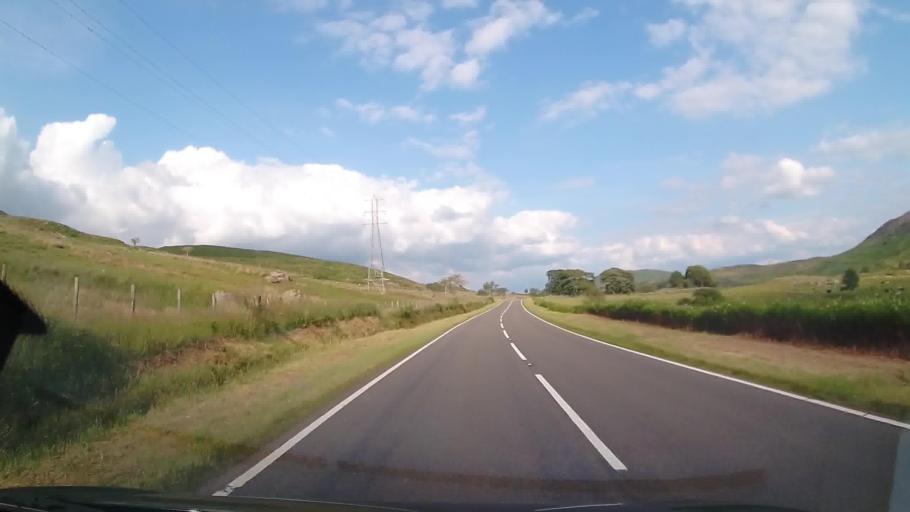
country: GB
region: Wales
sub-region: Gwynedd
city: Bala
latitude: 52.9447
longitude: -3.7471
